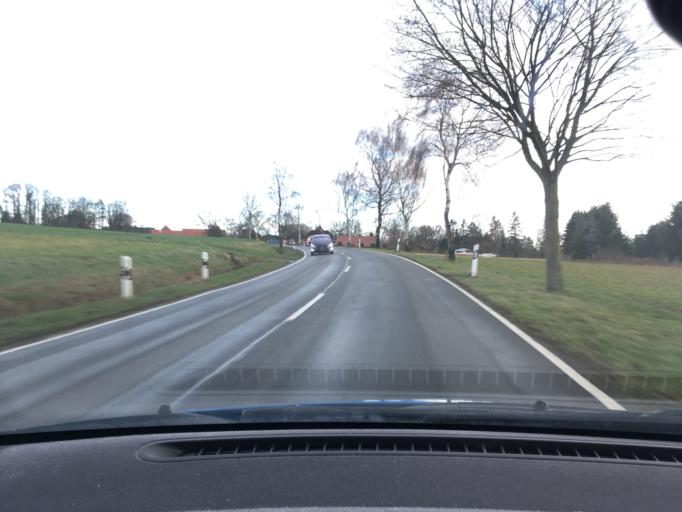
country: DE
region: Lower Saxony
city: Egestorf
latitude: 53.2149
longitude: 10.0285
